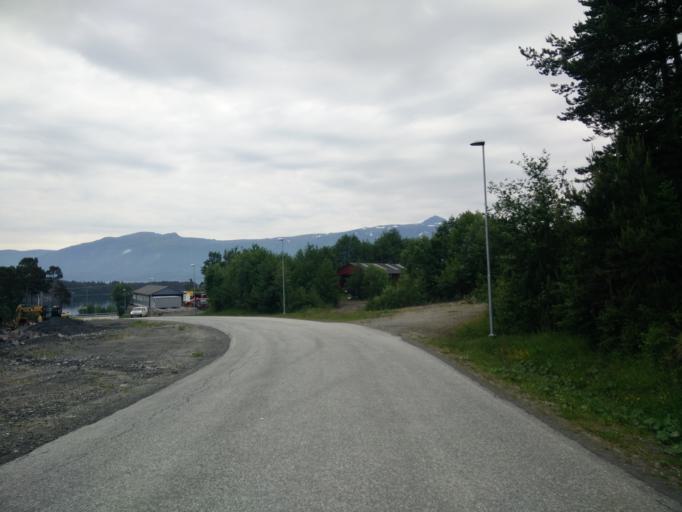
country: NO
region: More og Romsdal
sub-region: Kristiansund
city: Rensvik
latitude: 63.0132
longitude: 7.9688
